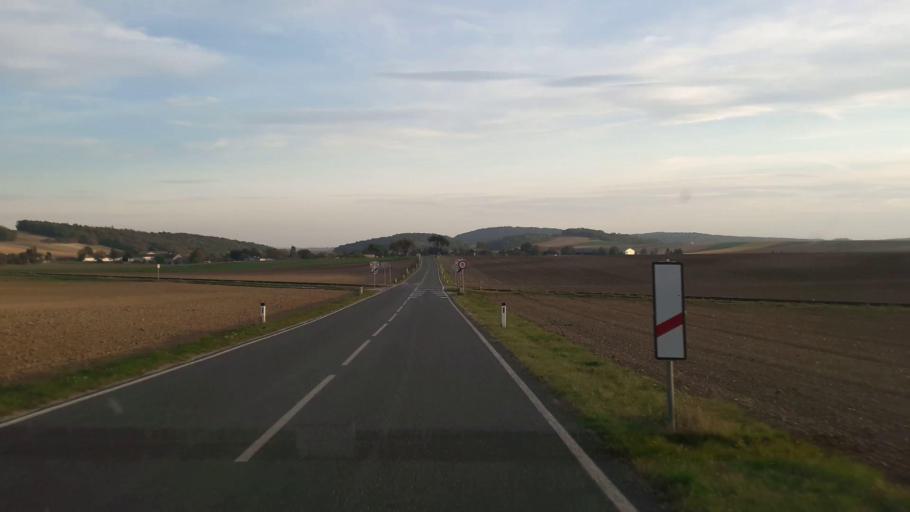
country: AT
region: Lower Austria
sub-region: Politischer Bezirk Korneuburg
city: Ernstbrunn
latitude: 48.5050
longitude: 16.3627
